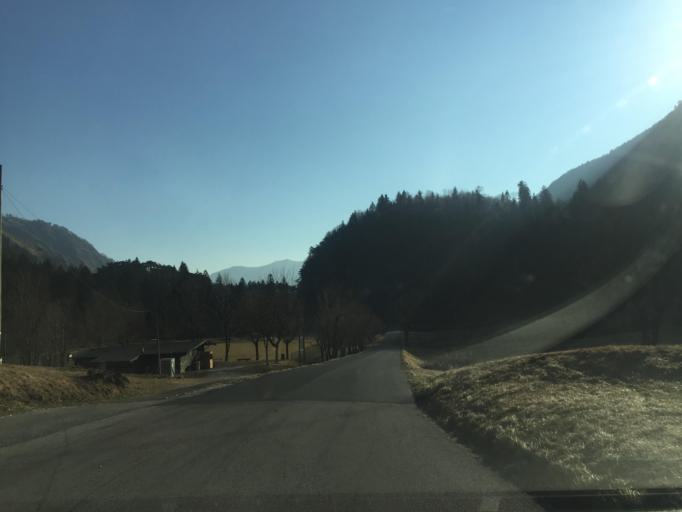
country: IT
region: Friuli Venezia Giulia
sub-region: Provincia di Udine
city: Tolmezzo
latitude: 46.4225
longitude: 13.0515
